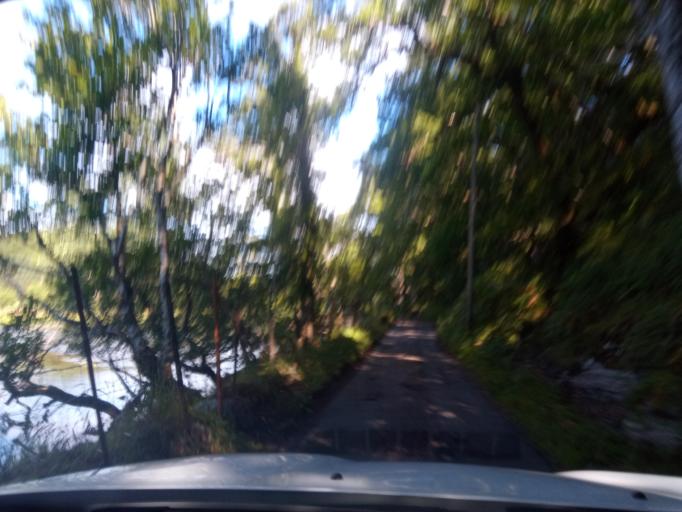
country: GB
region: Scotland
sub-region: Argyll and Bute
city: Isle Of Mull
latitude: 56.7612
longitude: -5.8183
